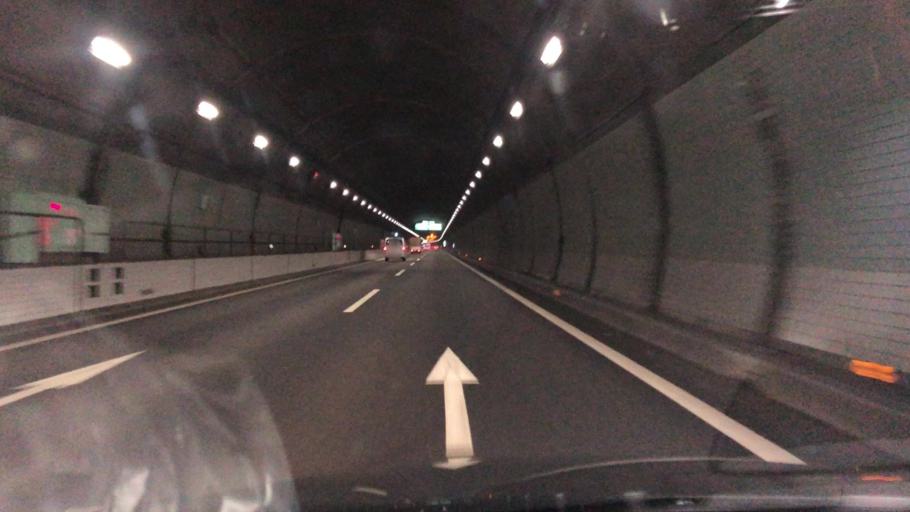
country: JP
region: Tokyo
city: Hachioji
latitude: 35.6558
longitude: 139.2499
